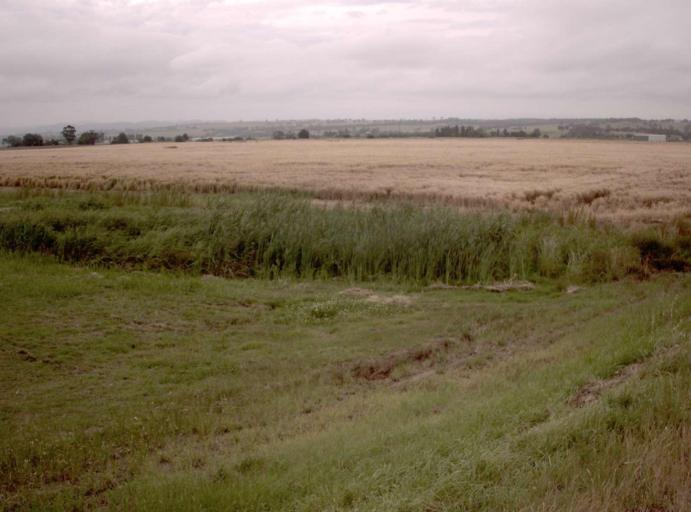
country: AU
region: Victoria
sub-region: East Gippsland
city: Bairnsdale
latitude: -37.7956
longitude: 147.4405
